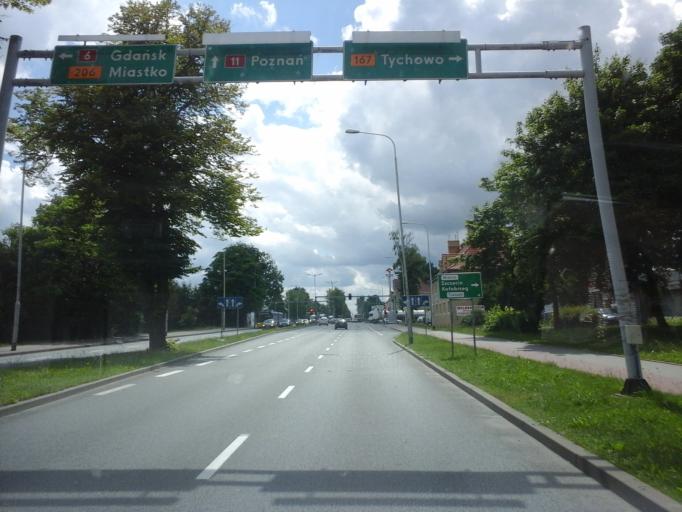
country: PL
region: West Pomeranian Voivodeship
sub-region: Koszalin
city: Koszalin
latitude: 54.1797
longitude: 16.1946
